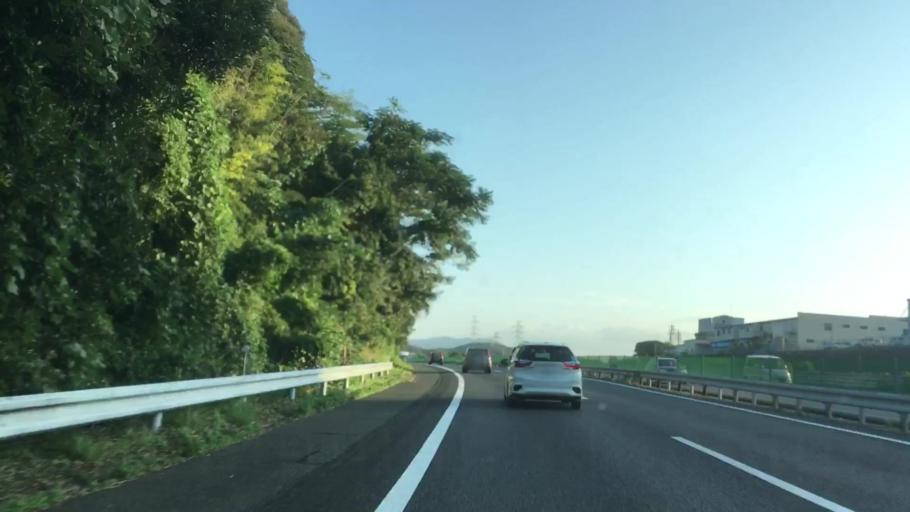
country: JP
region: Yamaguchi
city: Shimonoseki
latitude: 33.9866
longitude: 130.9512
